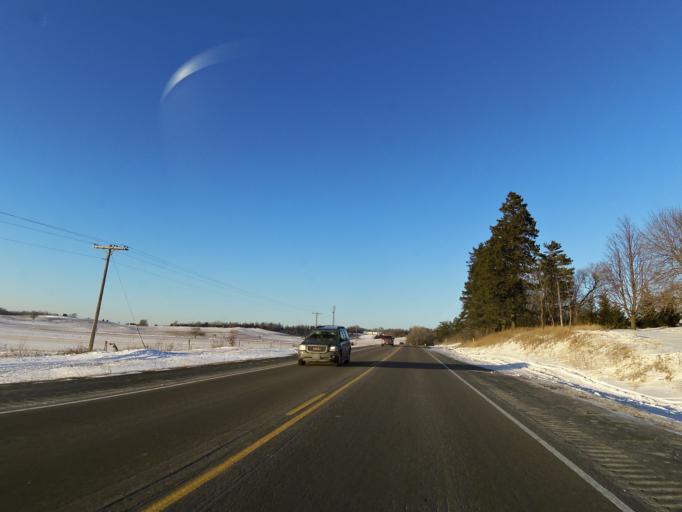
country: US
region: Minnesota
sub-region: Dakota County
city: Farmington
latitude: 44.5514
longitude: -93.1367
